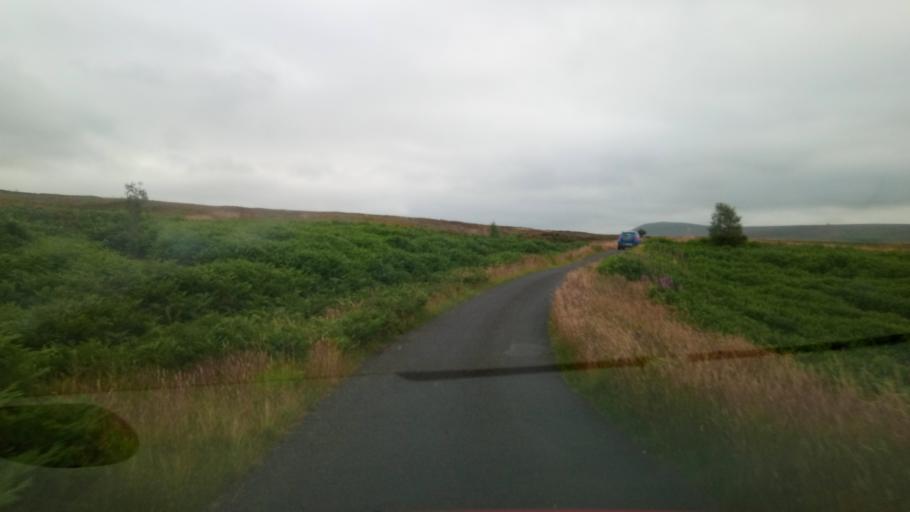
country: GB
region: Scotland
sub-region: Dumfries and Galloway
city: Langholm
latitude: 55.1704
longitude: -2.9530
